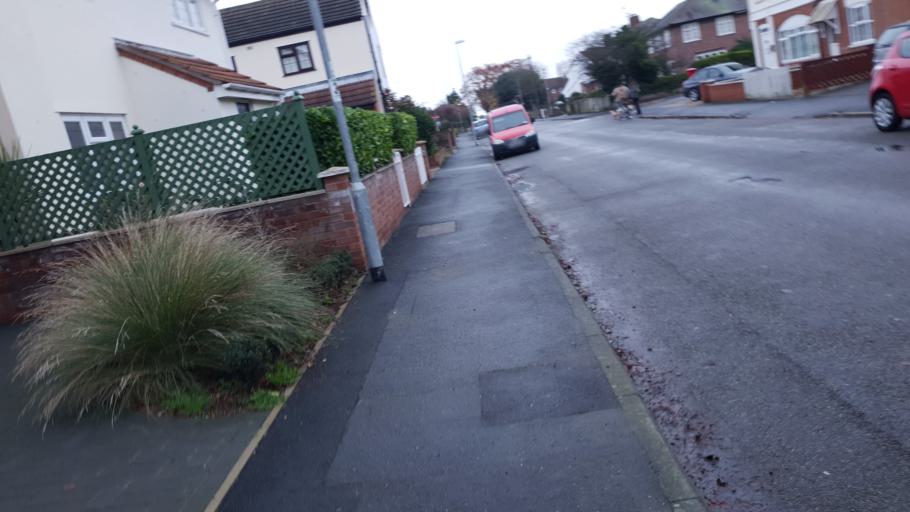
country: GB
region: England
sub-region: Essex
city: Frinton-on-Sea
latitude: 51.8373
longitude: 1.2511
